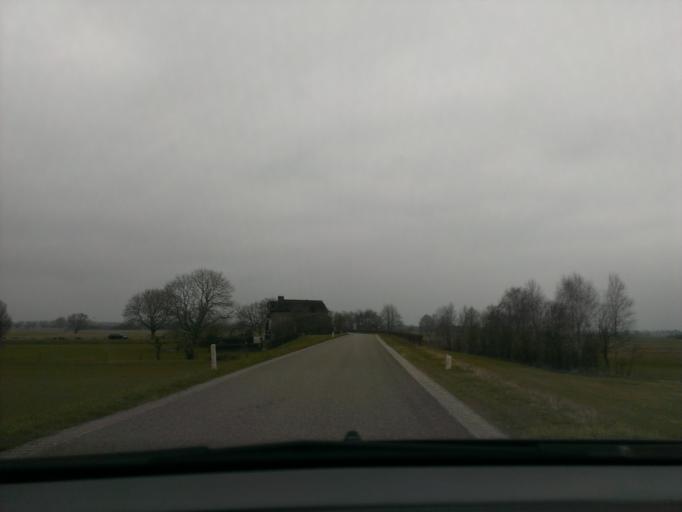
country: NL
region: Overijssel
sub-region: Gemeente Olst-Wijhe
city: Wijhe
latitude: 52.3945
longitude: 6.1237
